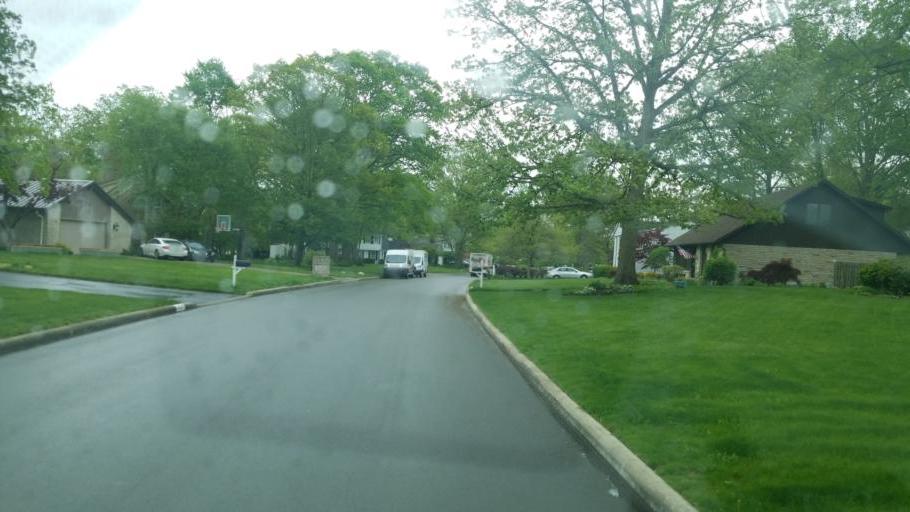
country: US
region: Ohio
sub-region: Delaware County
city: Powell
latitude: 40.1314
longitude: -83.0563
